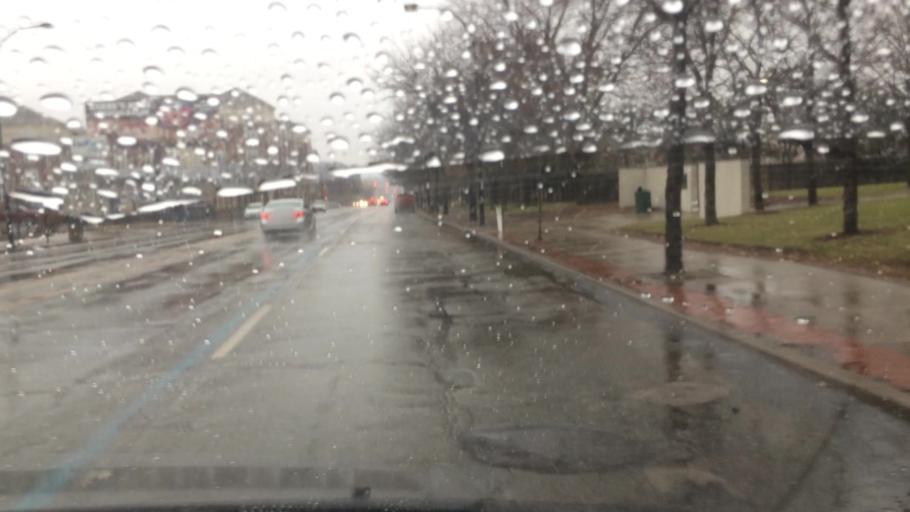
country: US
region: Ohio
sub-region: Summit County
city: Akron
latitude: 41.0722
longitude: -81.5110
